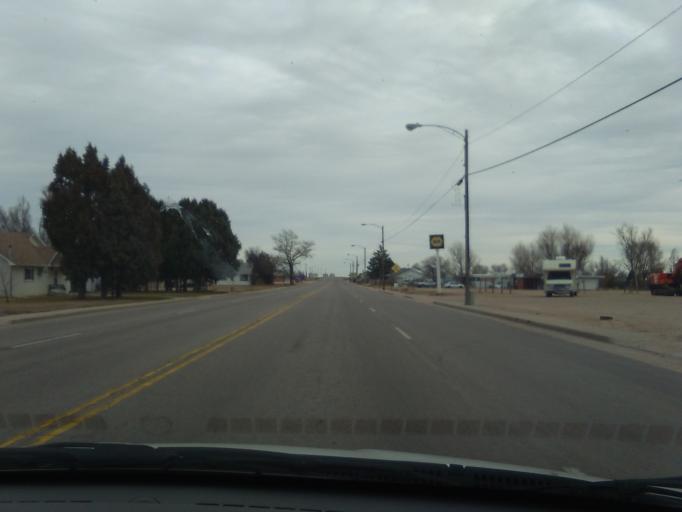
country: US
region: Colorado
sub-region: Washington County
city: Akron
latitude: 40.1592
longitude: -103.2096
